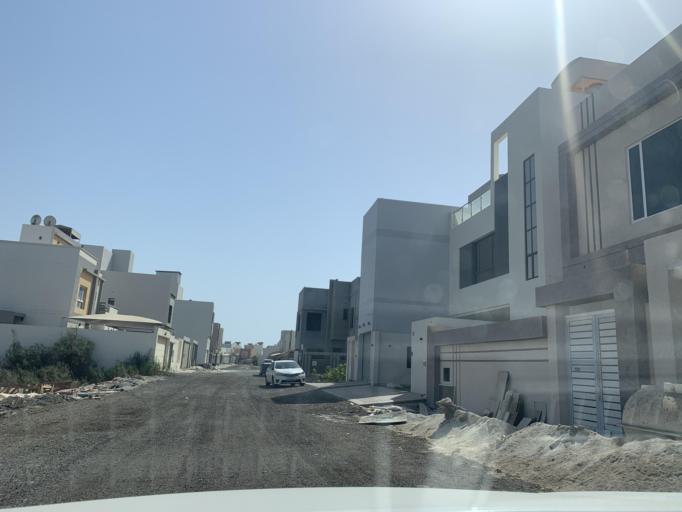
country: BH
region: Manama
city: Jidd Hafs
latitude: 26.2321
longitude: 50.4701
